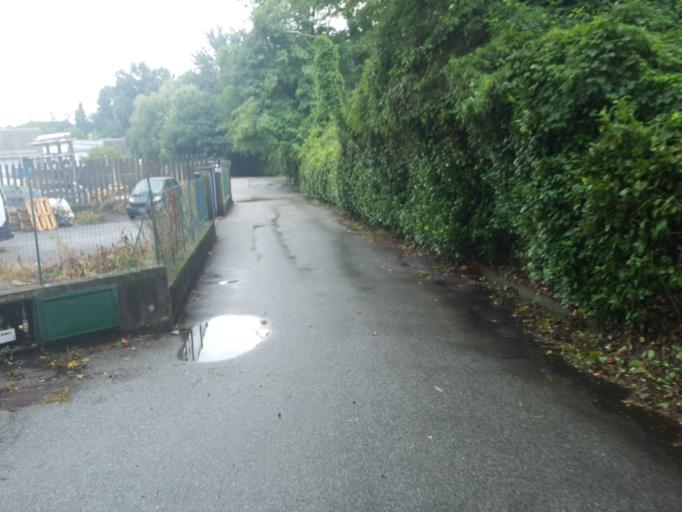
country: IT
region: Piedmont
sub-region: Provincia Verbano-Cusio-Ossola
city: Cambiasca
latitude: 45.9533
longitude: 8.5522
